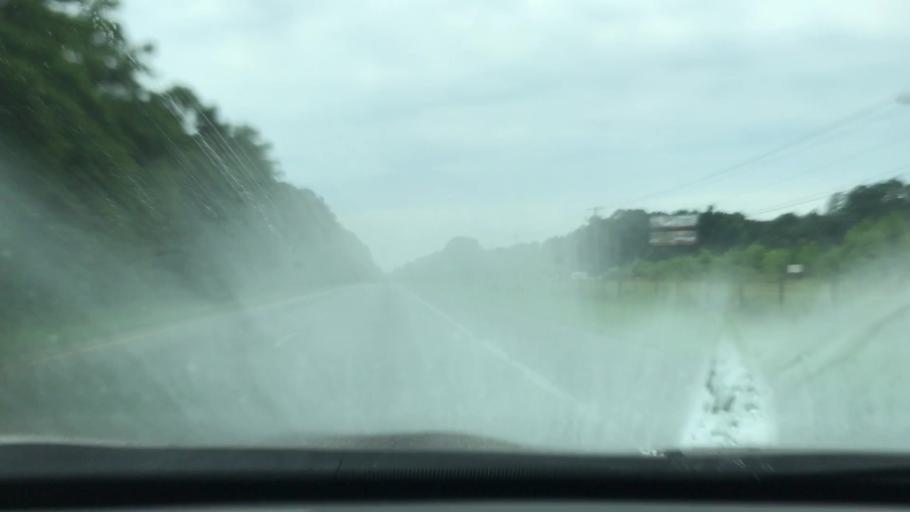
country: US
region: South Carolina
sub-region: Jasper County
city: Ridgeland
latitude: 32.5263
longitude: -80.9608
